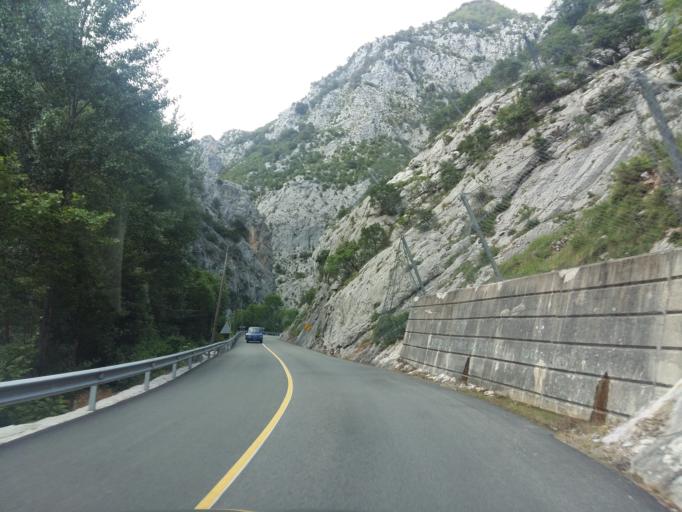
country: ES
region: Cantabria
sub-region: Provincia de Cantabria
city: Potes
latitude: 43.2331
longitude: -4.5786
